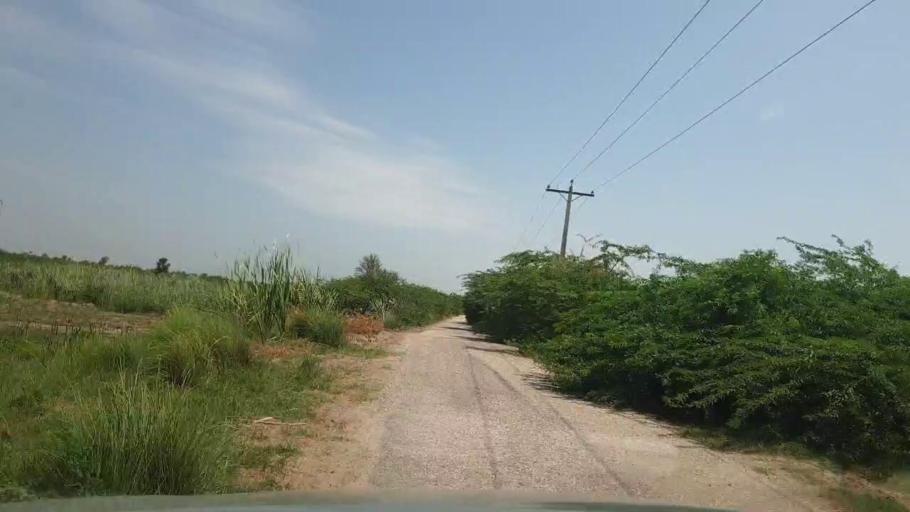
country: PK
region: Sindh
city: Bozdar
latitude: 27.1019
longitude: 68.9769
